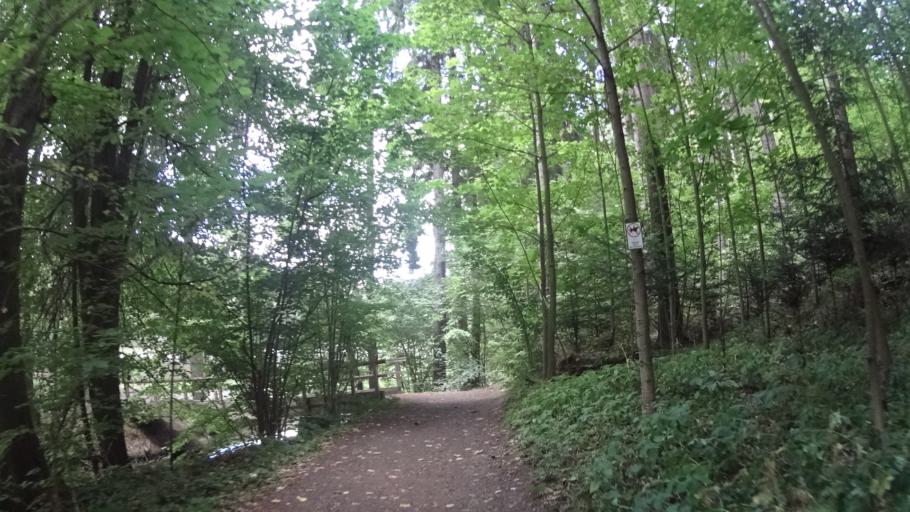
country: CZ
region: Pardubicky
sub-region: Okres Usti nad Orlici
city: Lanskroun
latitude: 49.9237
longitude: 16.5688
